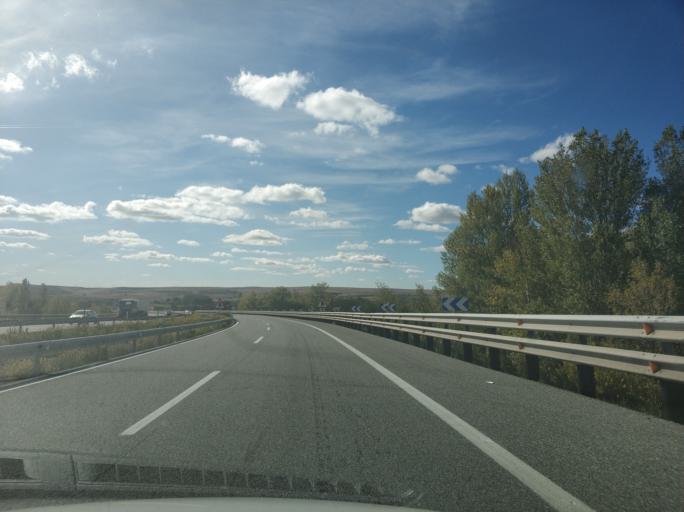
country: ES
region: Castille and Leon
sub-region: Provincia de Burgos
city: Buniel
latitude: 42.3109
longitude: -3.8161
